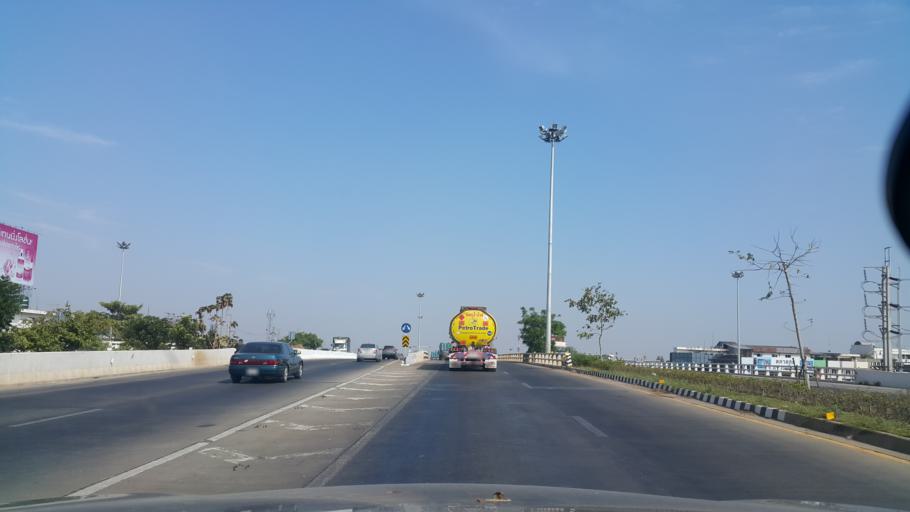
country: TH
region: Nakhon Ratchasima
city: Nakhon Ratchasima
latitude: 14.9581
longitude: 102.0535
